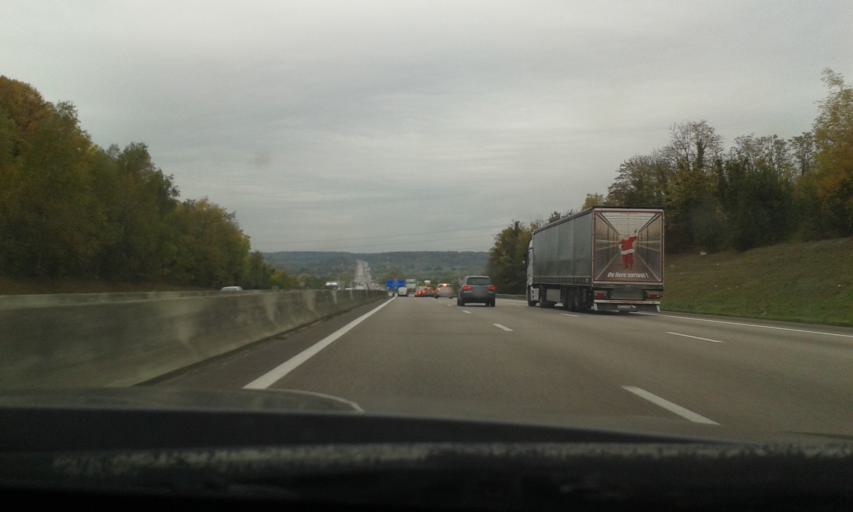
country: FR
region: Haute-Normandie
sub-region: Departement de la Seine-Maritime
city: Tourville-la-Riviere
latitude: 49.3227
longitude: 1.0991
